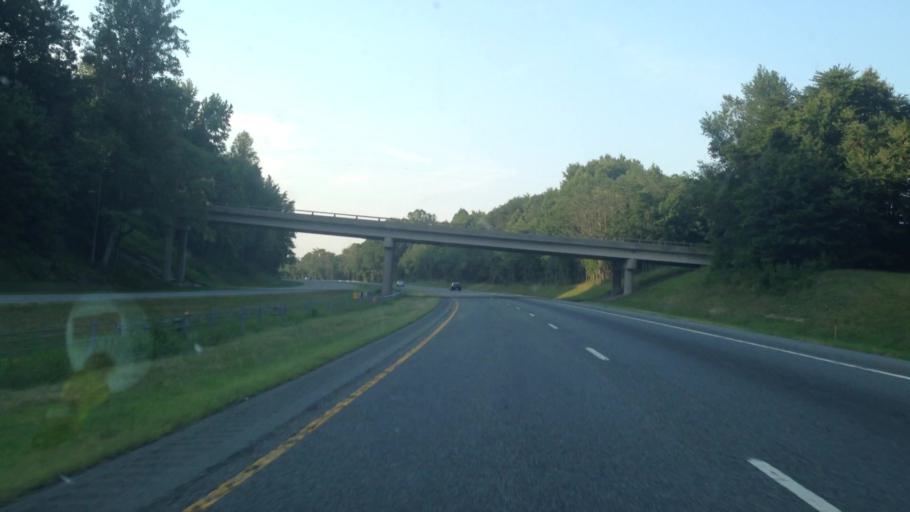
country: US
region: North Carolina
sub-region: Rockingham County
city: Reidsville
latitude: 36.4259
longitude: -79.5737
